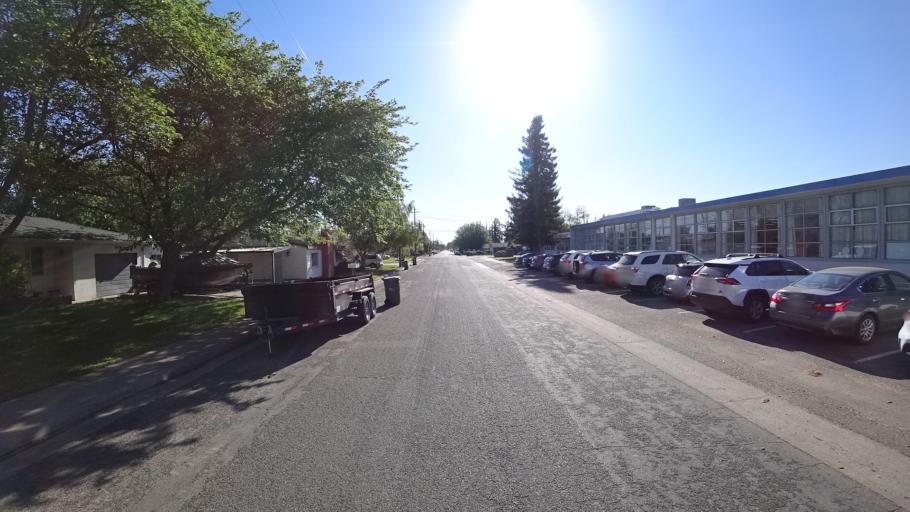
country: US
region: California
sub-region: Glenn County
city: Orland
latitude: 39.7416
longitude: -122.1932
